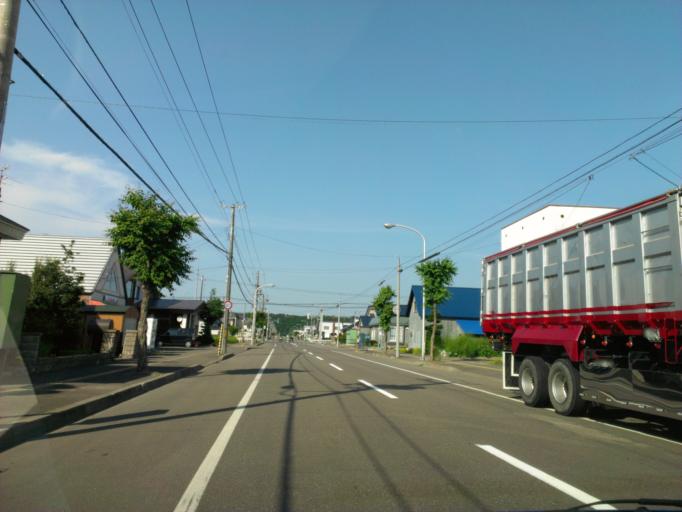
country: JP
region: Hokkaido
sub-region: Asahikawa-shi
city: Asahikawa
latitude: 43.5900
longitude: 142.4704
